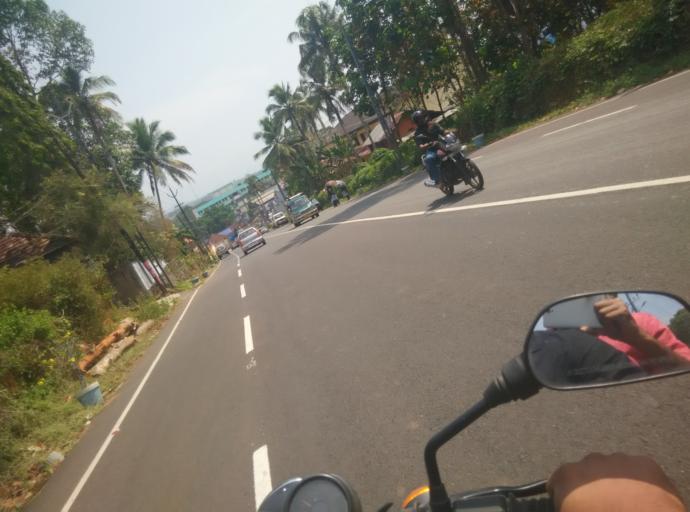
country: IN
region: Kerala
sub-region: Kottayam
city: Lalam
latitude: 9.7151
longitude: 76.6809
